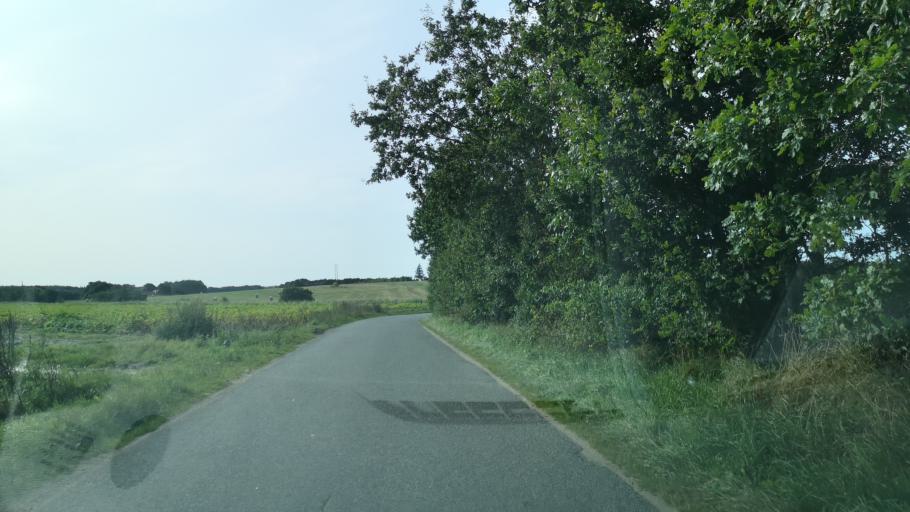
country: DK
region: Central Jutland
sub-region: Ikast-Brande Kommune
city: Ikast
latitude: 56.1558
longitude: 9.1183
